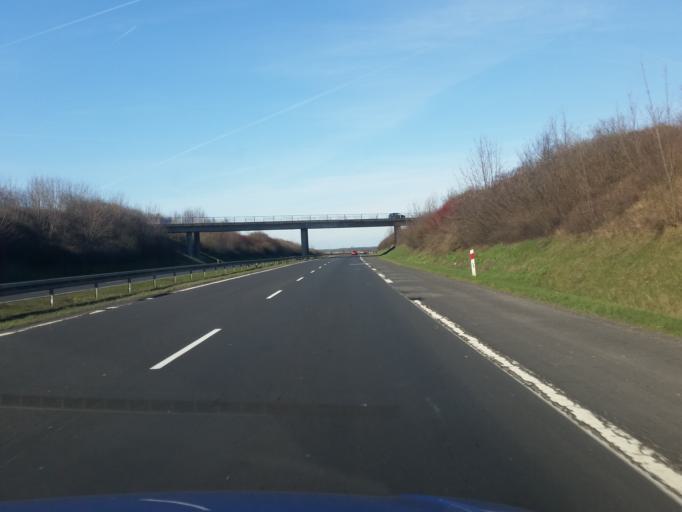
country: PL
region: Lodz Voivodeship
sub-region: Powiat radomszczanski
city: Kamiensk
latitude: 51.1928
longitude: 19.4735
